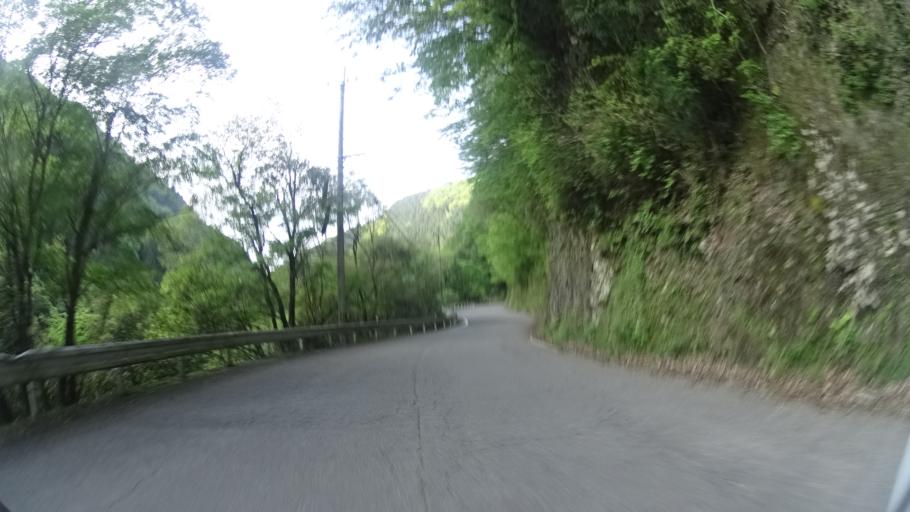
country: JP
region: Tokushima
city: Ikedacho
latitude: 33.8968
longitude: 133.8142
